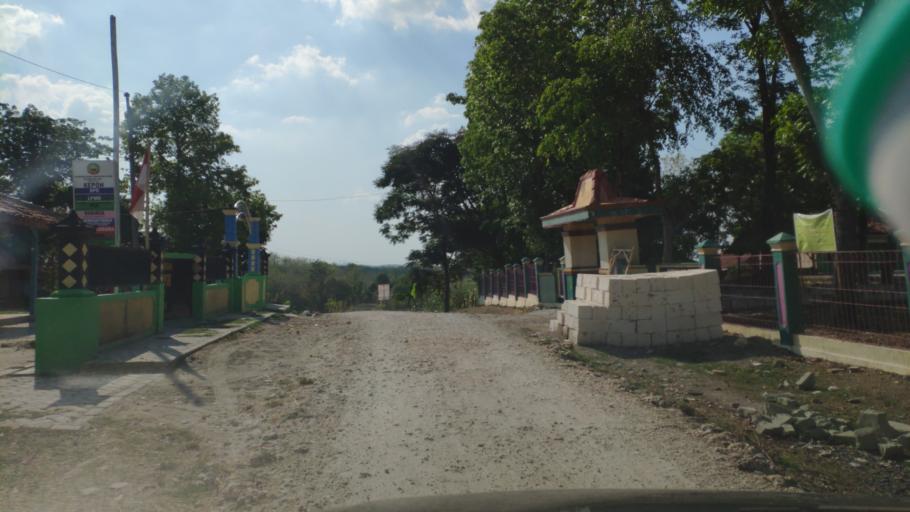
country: ID
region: Central Java
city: Randublatung
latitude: -7.2281
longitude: 111.3390
